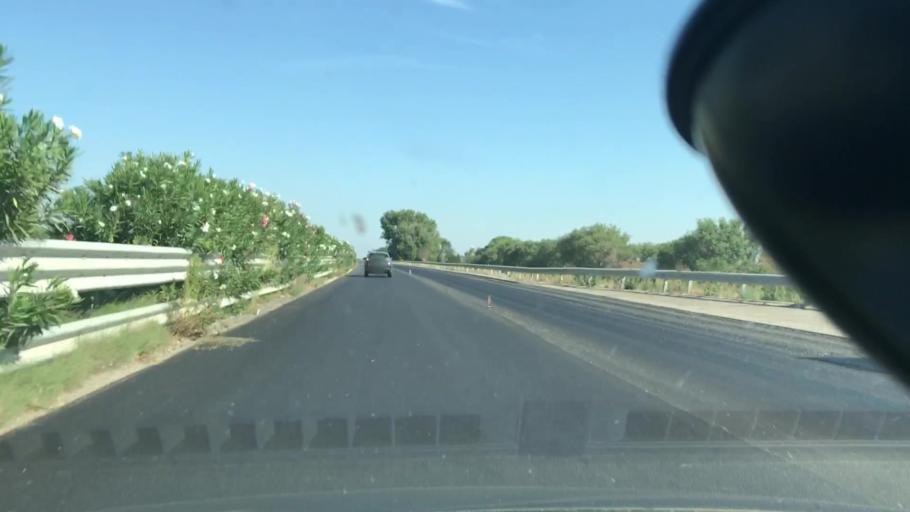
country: IT
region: Apulia
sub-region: Provincia di Foggia
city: Ascoli Satriano
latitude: 41.2721
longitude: 15.5528
